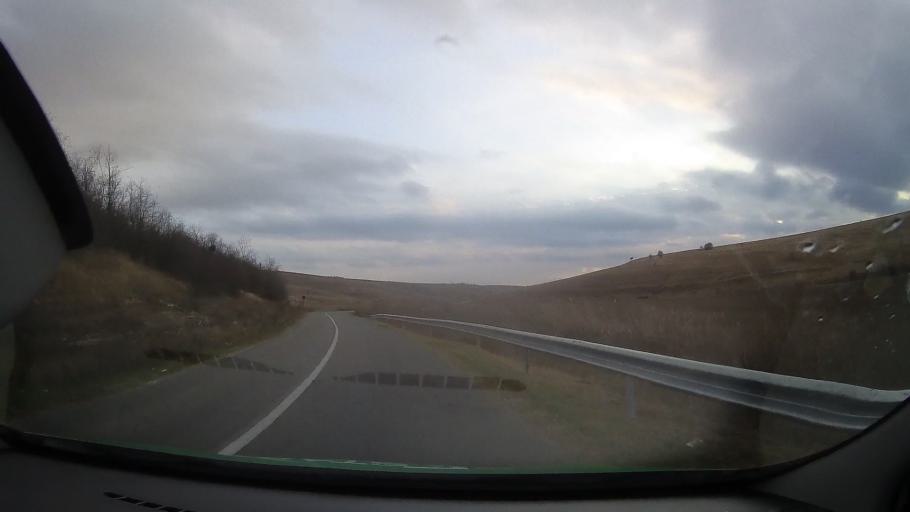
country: RO
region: Constanta
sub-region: Comuna Dobromir
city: Dobromir
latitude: 44.0362
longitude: 27.8025
